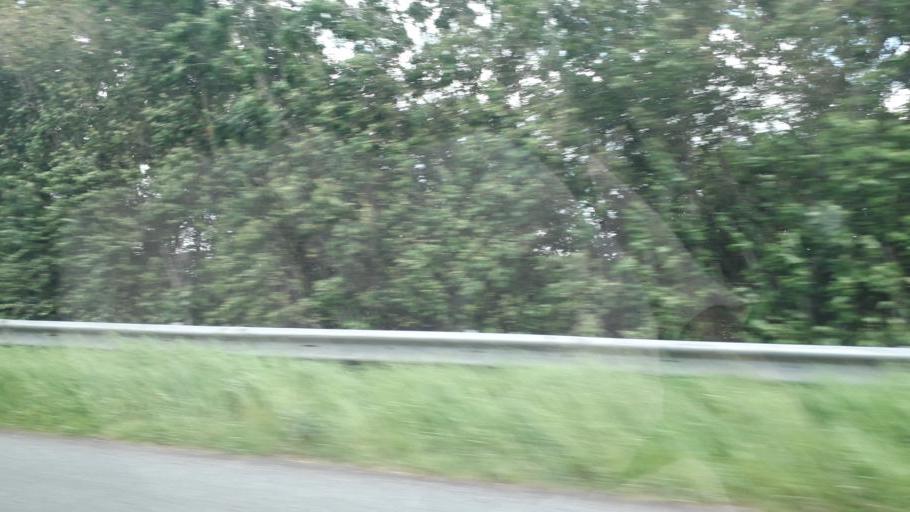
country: IE
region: Leinster
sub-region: Kildare
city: Moone
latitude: 53.0040
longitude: -6.8049
